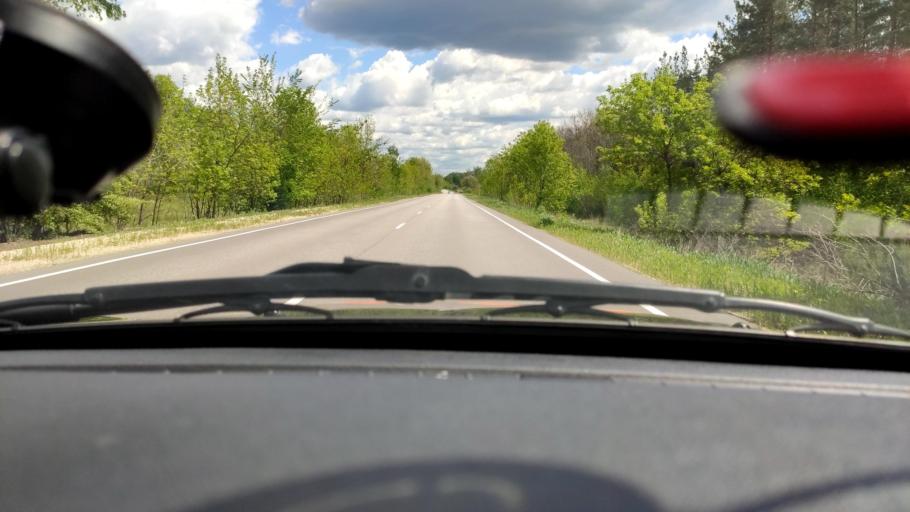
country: RU
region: Belgorod
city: Krasnoye
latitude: 51.0563
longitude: 38.8753
